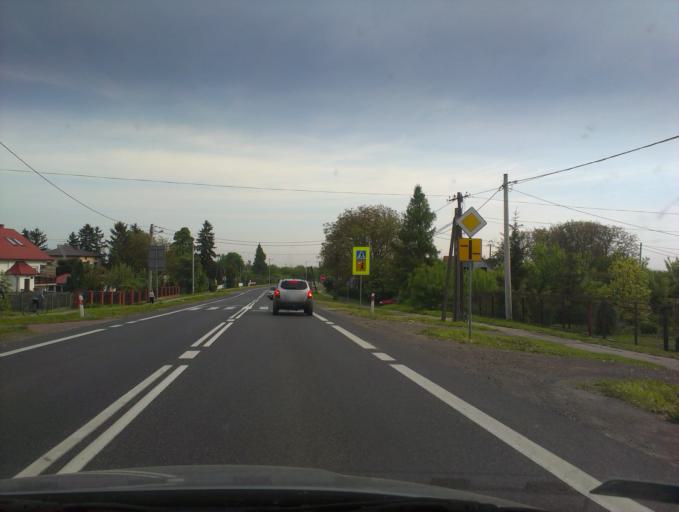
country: PL
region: Swietokrzyskie
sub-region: Powiat ostrowiecki
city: Ostrowiec Swietokrzyski
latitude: 50.8942
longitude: 21.3773
